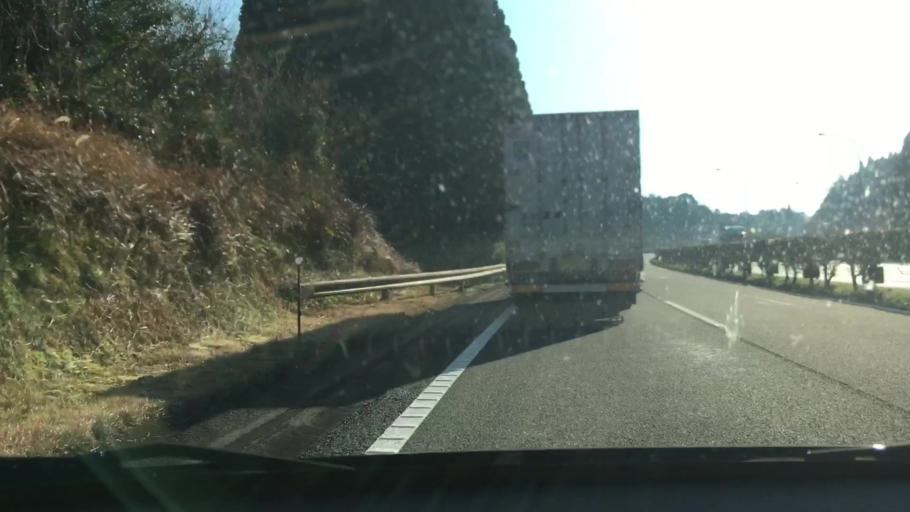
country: JP
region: Kagoshima
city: Kajiki
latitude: 31.8995
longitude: 130.7066
